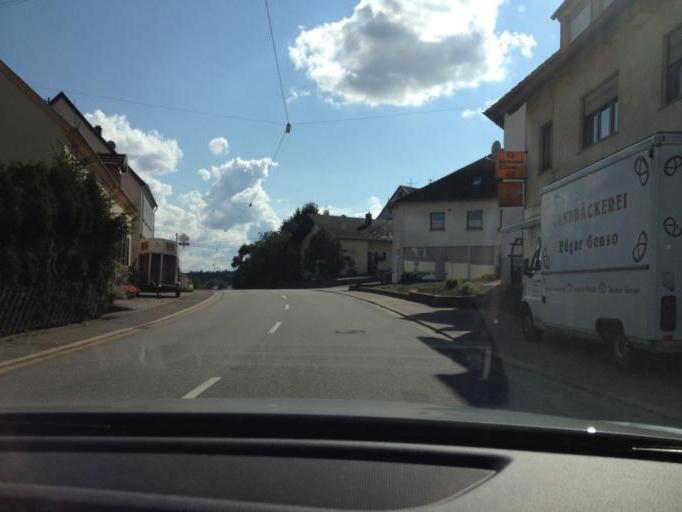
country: DE
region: Saarland
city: Marpingen
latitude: 49.4268
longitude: 7.0773
